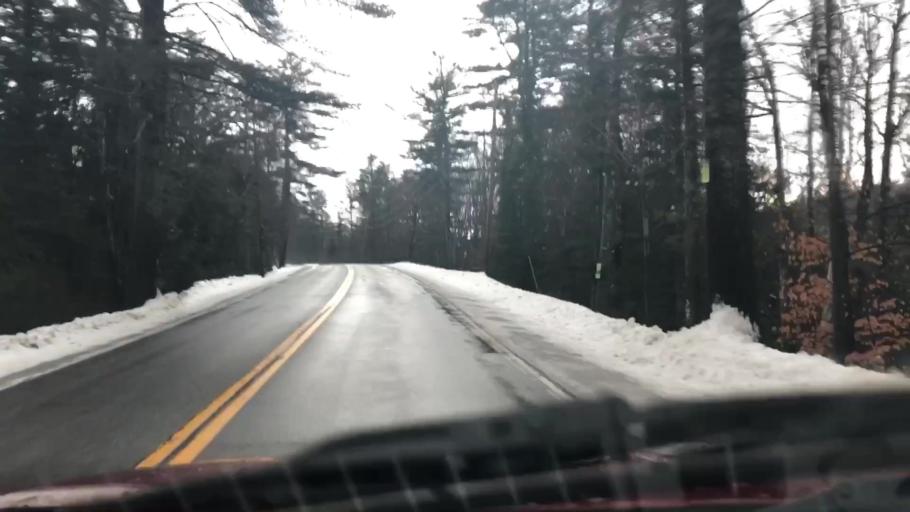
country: US
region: Maine
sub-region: Oxford County
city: West Paris
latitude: 44.4159
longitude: -70.6450
